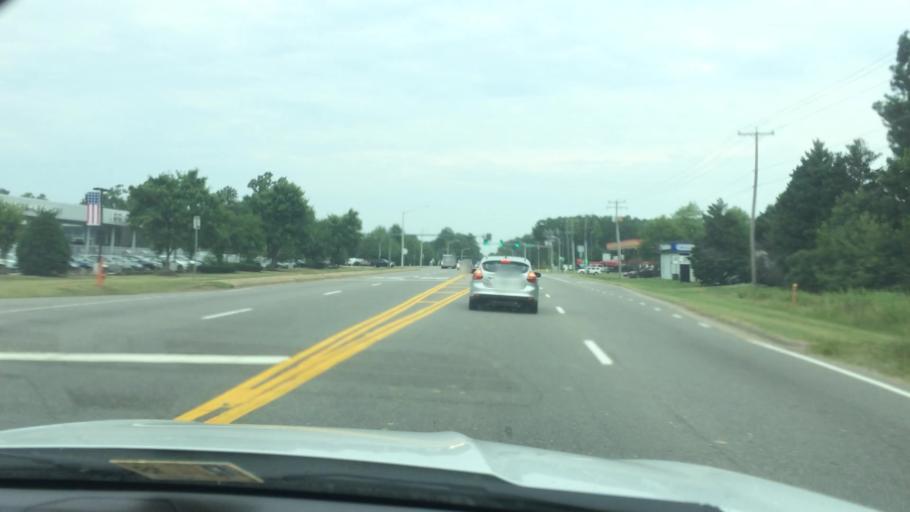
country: US
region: Virginia
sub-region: York County
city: Yorktown
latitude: 37.1636
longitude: -76.5396
